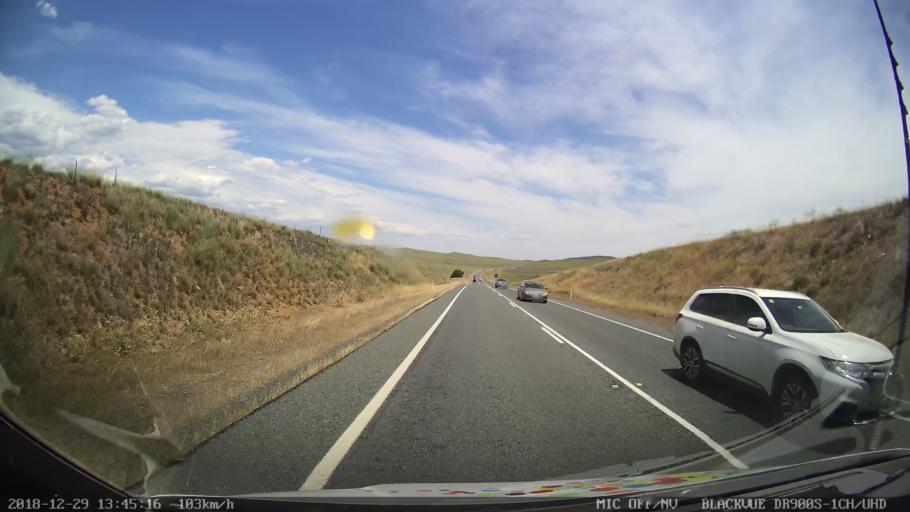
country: AU
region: New South Wales
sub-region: Cooma-Monaro
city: Cooma
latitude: -36.0939
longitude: 149.1452
